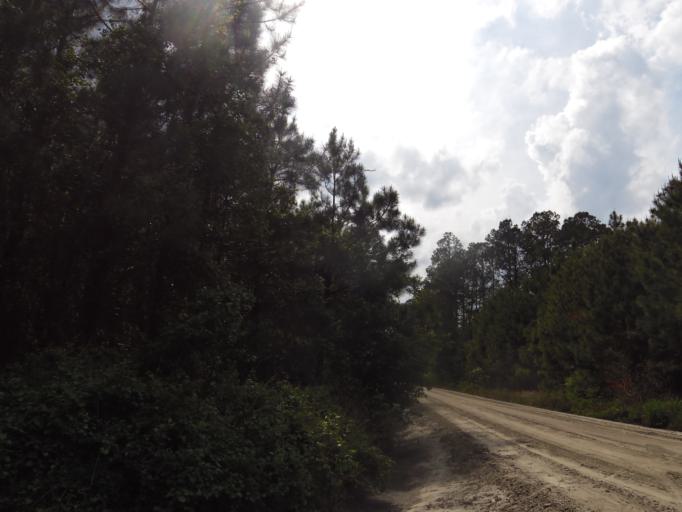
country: US
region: Georgia
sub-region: Charlton County
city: Folkston
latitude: 30.9411
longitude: -82.0237
